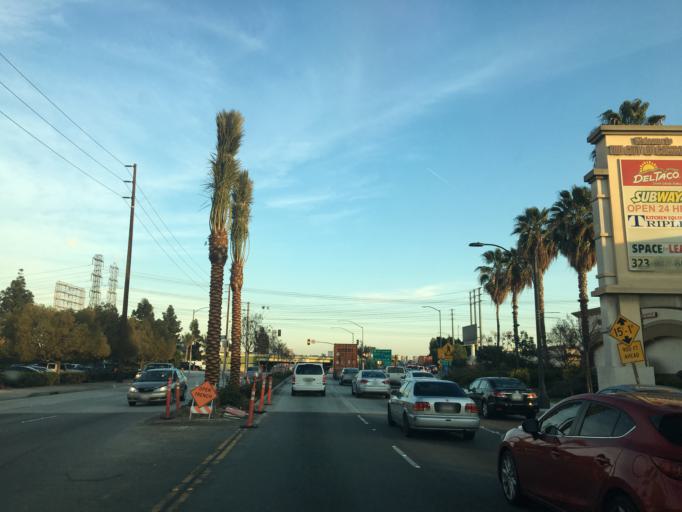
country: US
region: California
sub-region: Los Angeles County
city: Commerce
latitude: 33.9962
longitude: -118.1478
